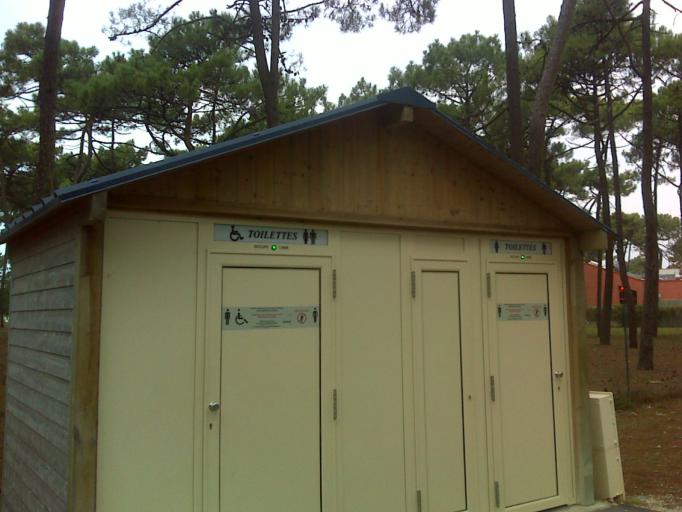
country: FR
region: Poitou-Charentes
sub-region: Departement de la Charente-Maritime
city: Les Mathes
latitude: 45.6768
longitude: -1.1616
